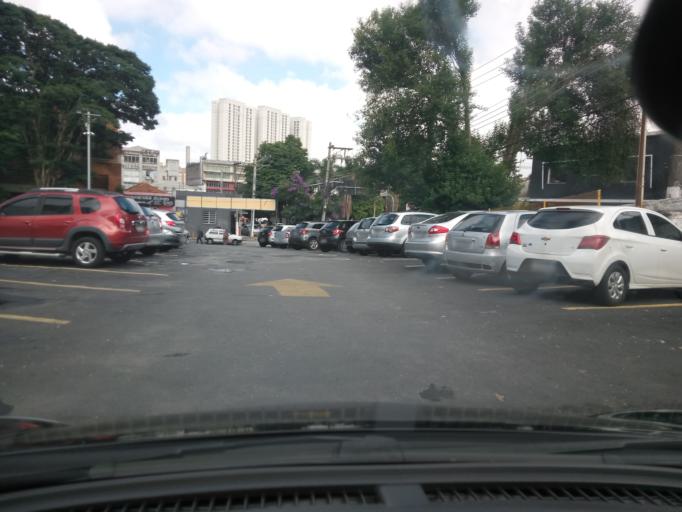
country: BR
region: Sao Paulo
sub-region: Sao Bernardo Do Campo
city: Sao Bernardo do Campo
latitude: -23.7039
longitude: -46.5503
